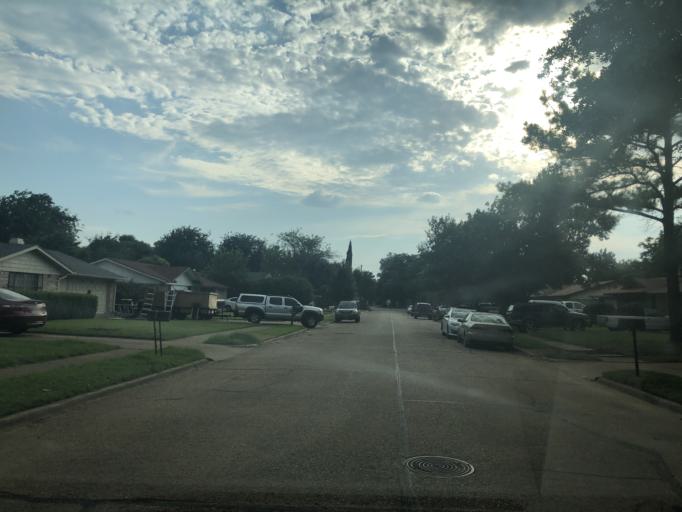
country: US
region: Texas
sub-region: Dallas County
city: Irving
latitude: 32.7876
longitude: -96.9757
